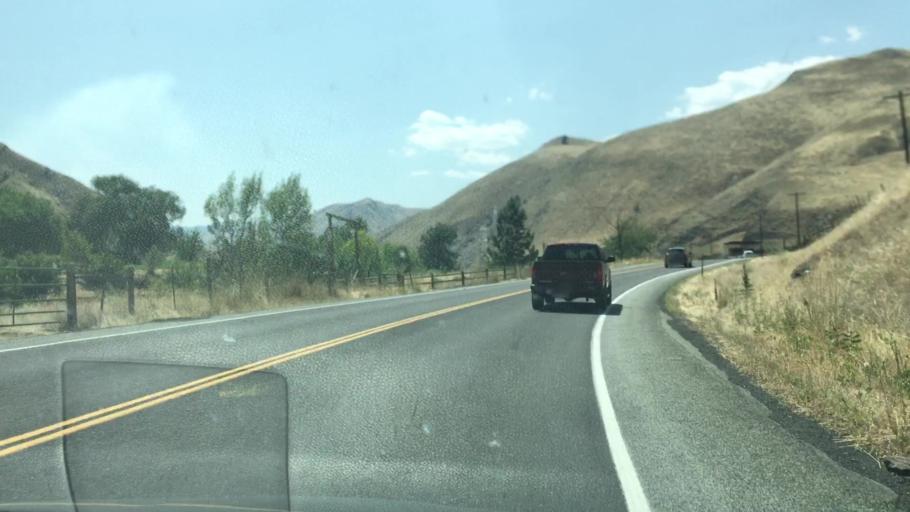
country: US
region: Idaho
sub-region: Valley County
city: McCall
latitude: 45.3937
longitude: -116.3427
